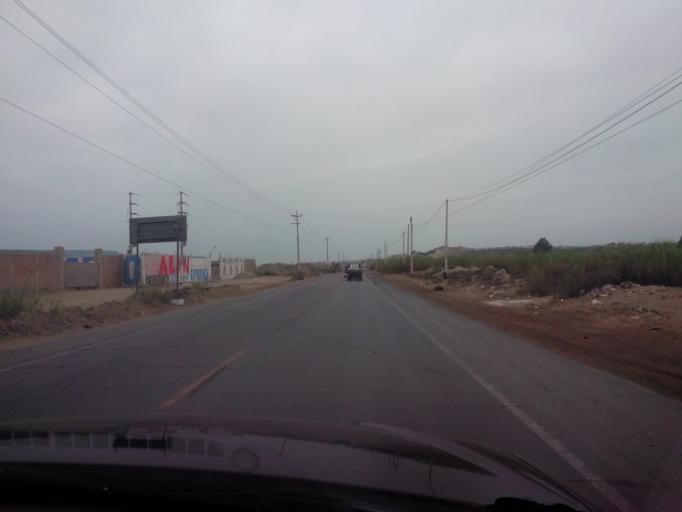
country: PE
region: Ica
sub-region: Provincia de Pisco
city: Villa Tupac Amaru
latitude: -13.6960
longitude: -76.1536
